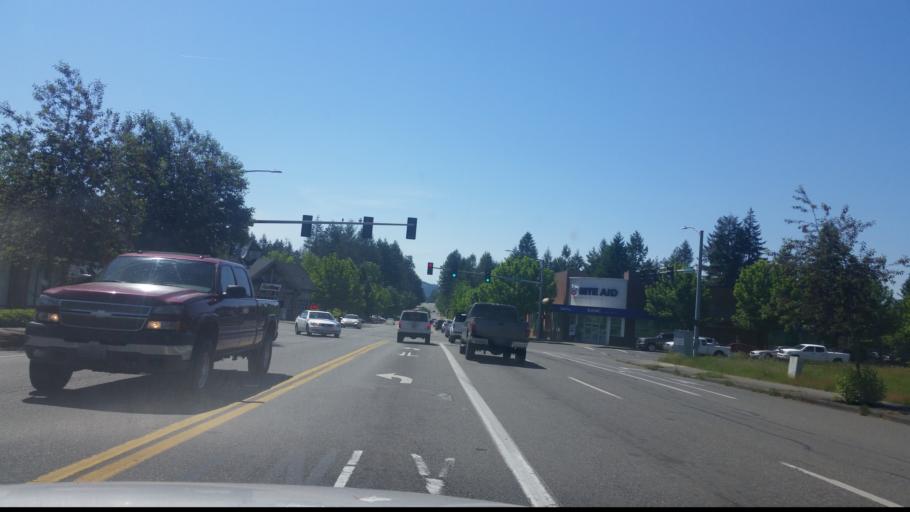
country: US
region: Washington
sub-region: Thurston County
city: Olympia
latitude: 47.0471
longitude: -122.9404
